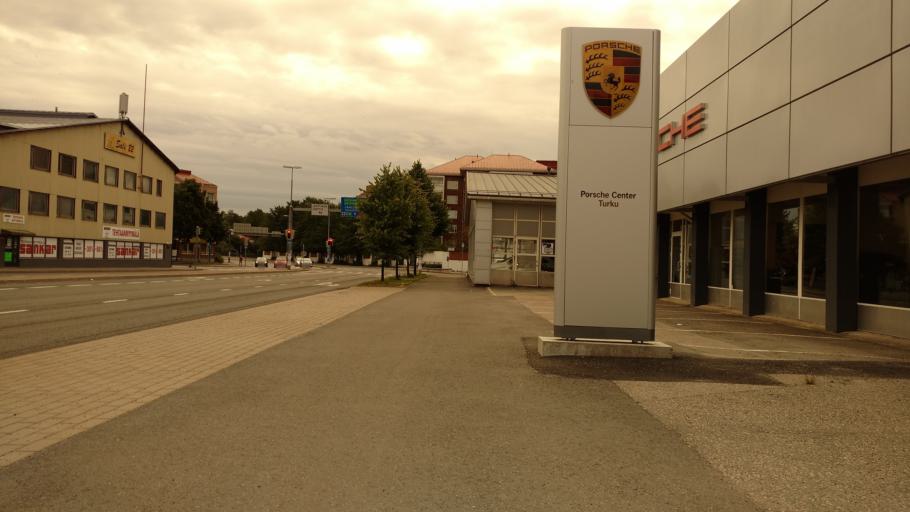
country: FI
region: Varsinais-Suomi
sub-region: Turku
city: Turku
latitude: 60.4591
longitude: 22.2726
